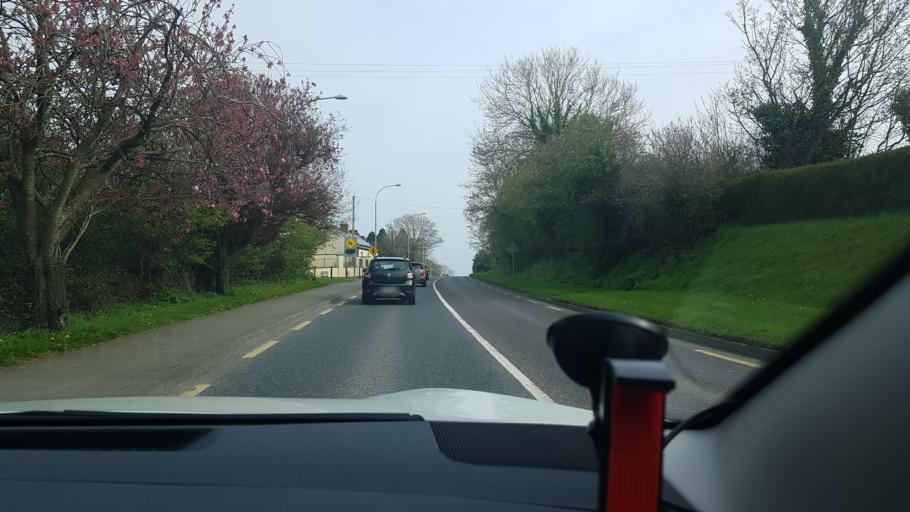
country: IE
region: Leinster
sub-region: An Mhi
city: Stamullin
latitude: 53.6692
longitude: -6.2808
